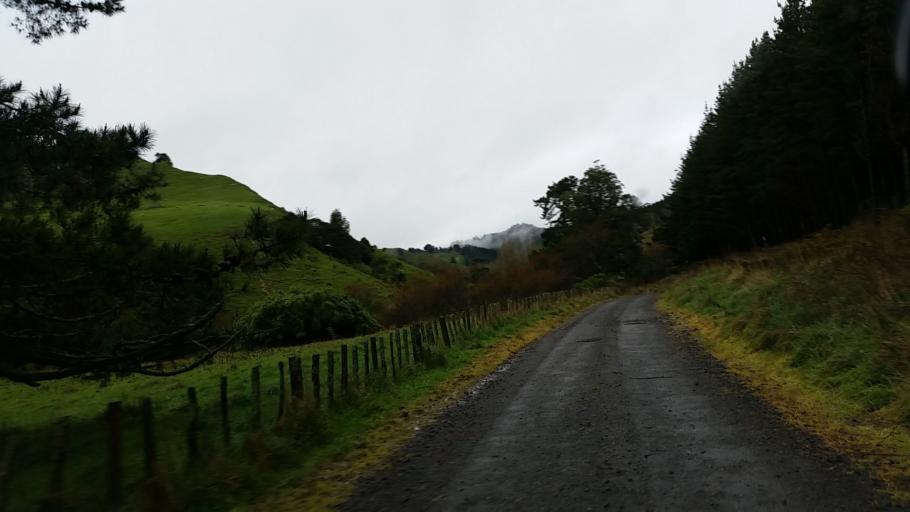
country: NZ
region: Taranaki
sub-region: South Taranaki District
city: Eltham
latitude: -39.5016
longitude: 174.4147
